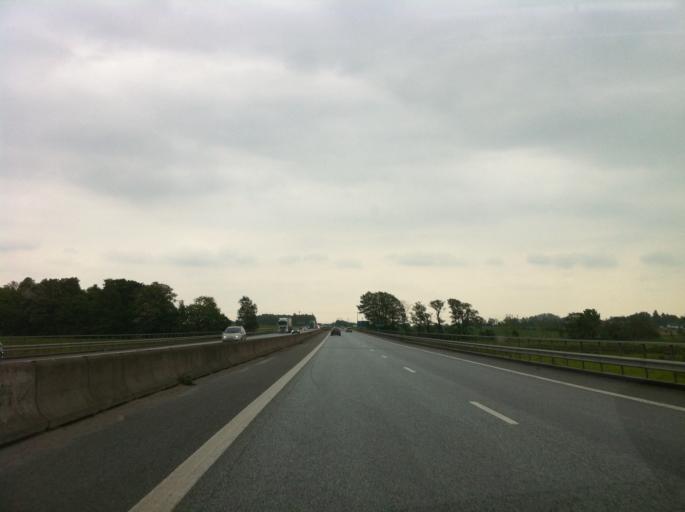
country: SE
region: Skane
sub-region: Kavlinge Kommun
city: Loddekopinge
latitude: 55.7515
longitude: 13.0088
